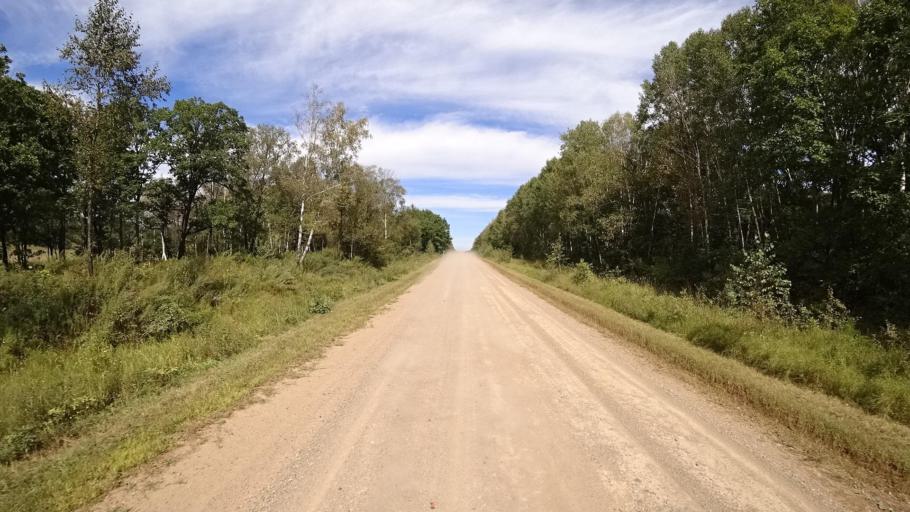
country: RU
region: Primorskiy
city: Yakovlevka
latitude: 44.6880
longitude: 133.6183
